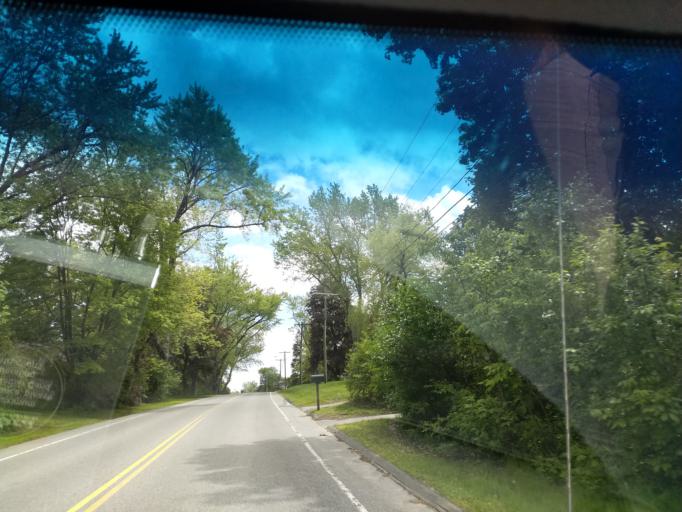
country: US
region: Maine
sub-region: Cumberland County
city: Falmouth
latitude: 43.7448
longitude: -70.2928
